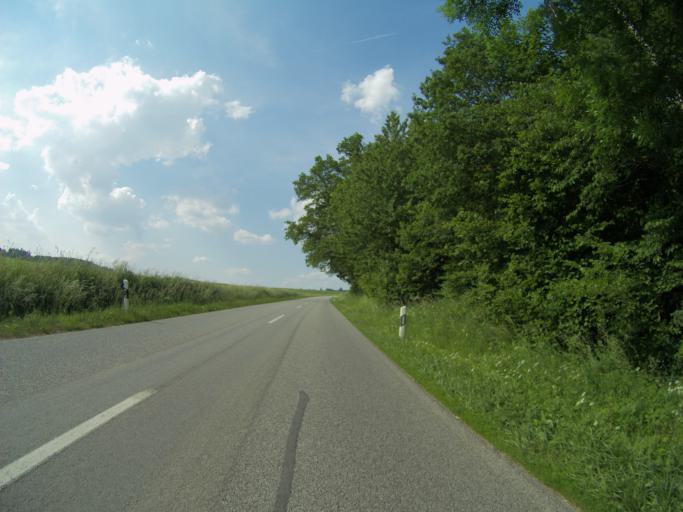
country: DE
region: Bavaria
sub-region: Upper Bavaria
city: Zolling
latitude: 48.4609
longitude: 11.7897
